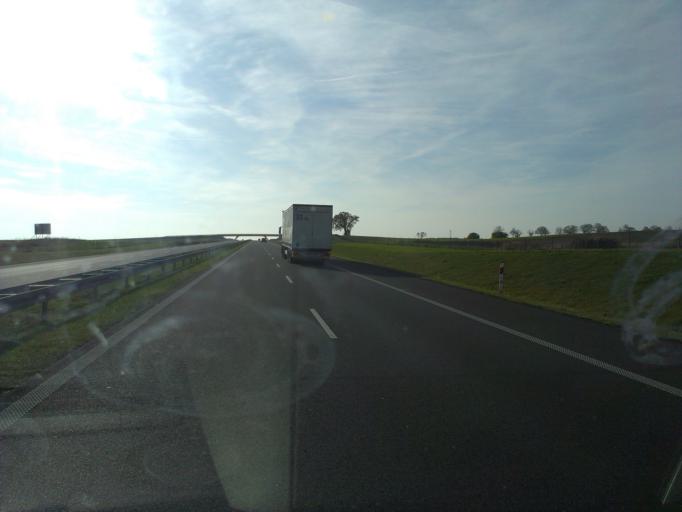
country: PL
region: West Pomeranian Voivodeship
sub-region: Powiat pyrzycki
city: Kozielice
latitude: 53.0366
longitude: 14.8646
